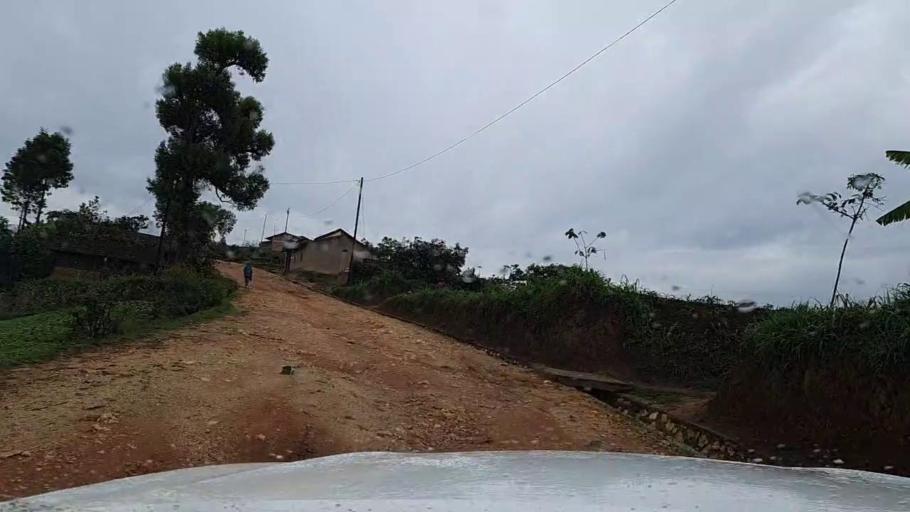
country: RW
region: Southern Province
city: Nzega
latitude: -2.4679
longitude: 29.4975
